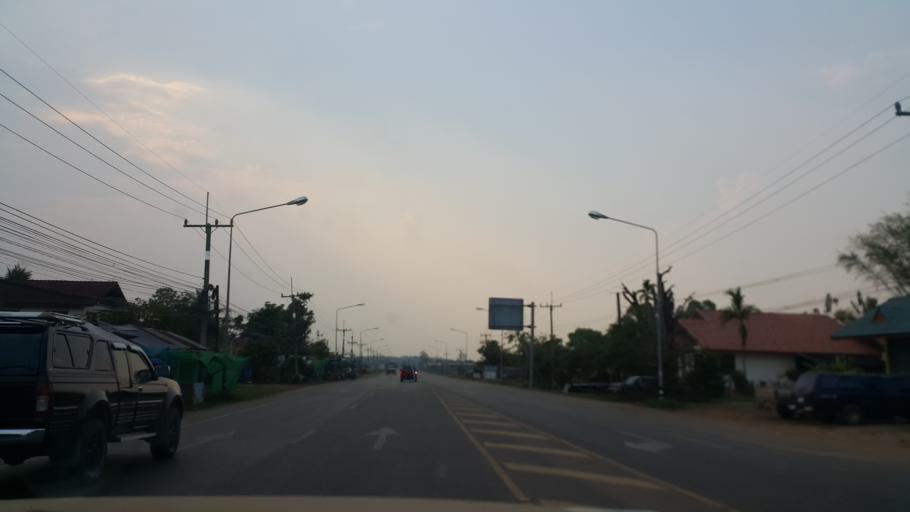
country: TH
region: Nakhon Phanom
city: Renu Nakhon
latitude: 17.0185
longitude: 104.7268
